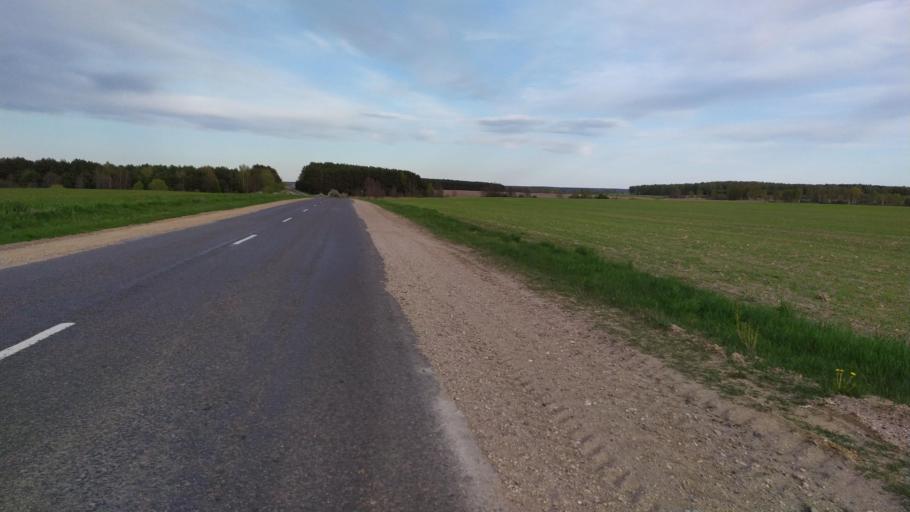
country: BY
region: Brest
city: Kamyanyets
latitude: 52.4102
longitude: 23.7258
